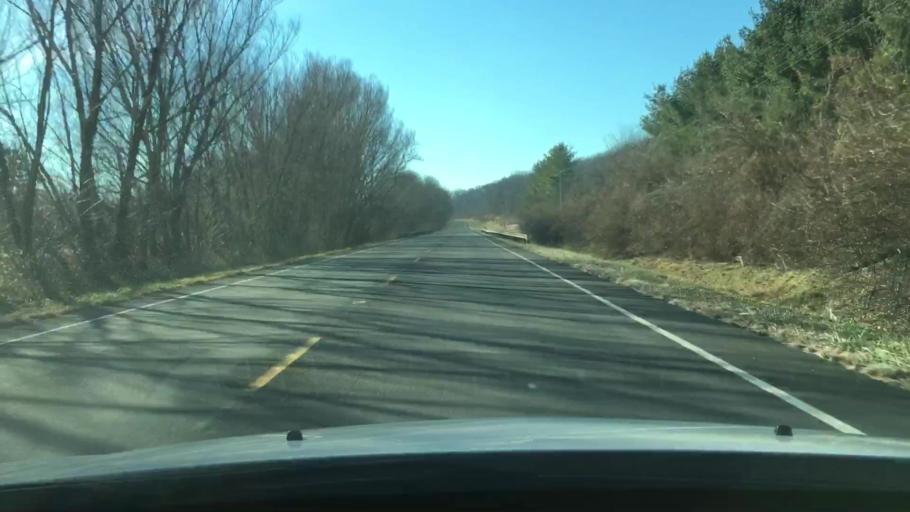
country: US
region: Illinois
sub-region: Fulton County
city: Canton
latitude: 40.4917
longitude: -89.9391
